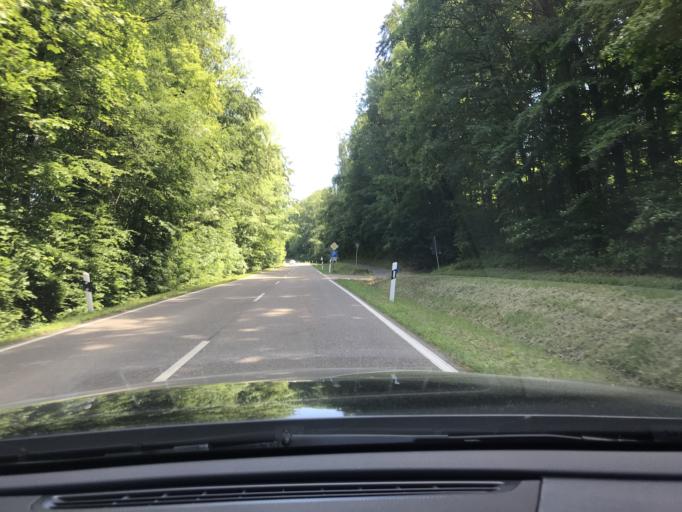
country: DE
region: Baden-Wuerttemberg
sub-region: Regierungsbezirk Stuttgart
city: Weinstadt-Endersbach
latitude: 48.7879
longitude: 9.3877
